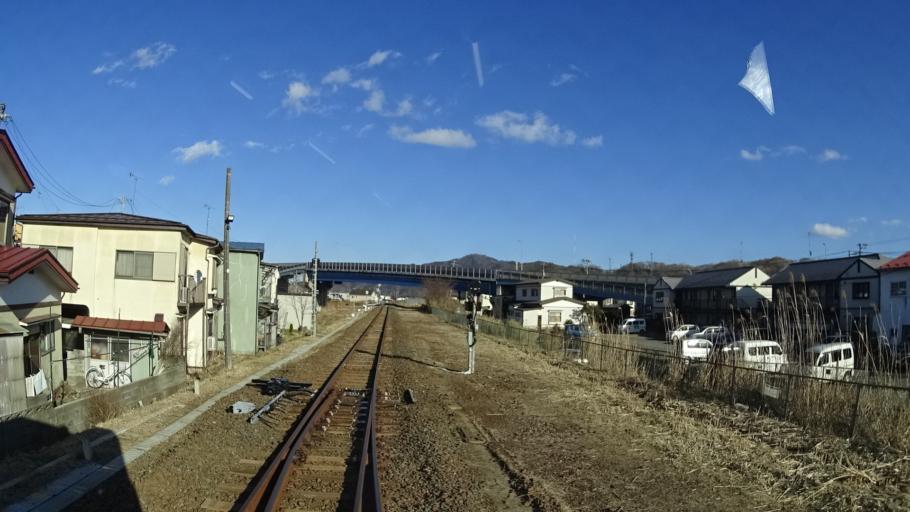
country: JP
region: Iwate
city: Miyako
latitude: 39.6394
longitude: 141.9504
